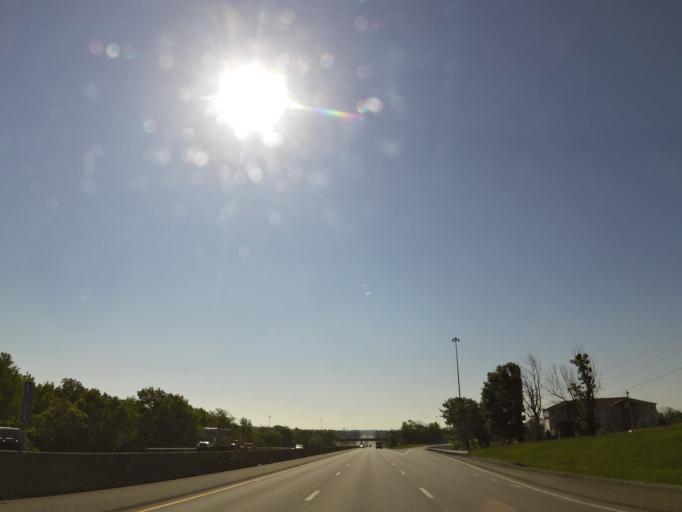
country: US
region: Kentucky
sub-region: Shelby County
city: Shelbyville
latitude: 38.1940
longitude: -85.2780
